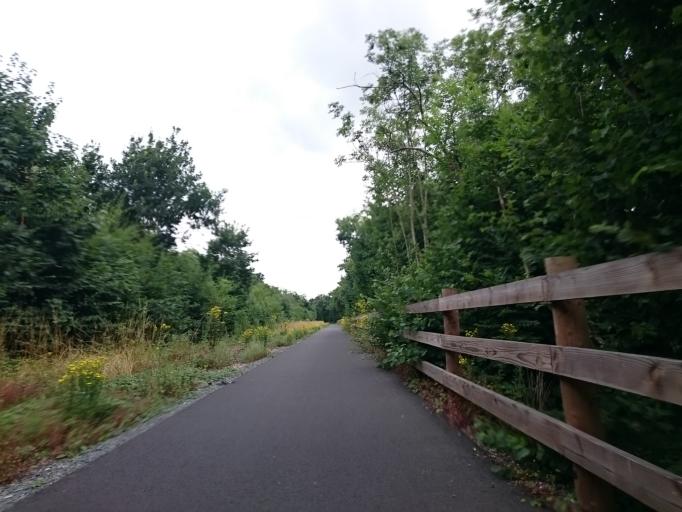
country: FR
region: Lower Normandy
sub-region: Departement du Calvados
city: Bully
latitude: 49.0918
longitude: -0.4187
